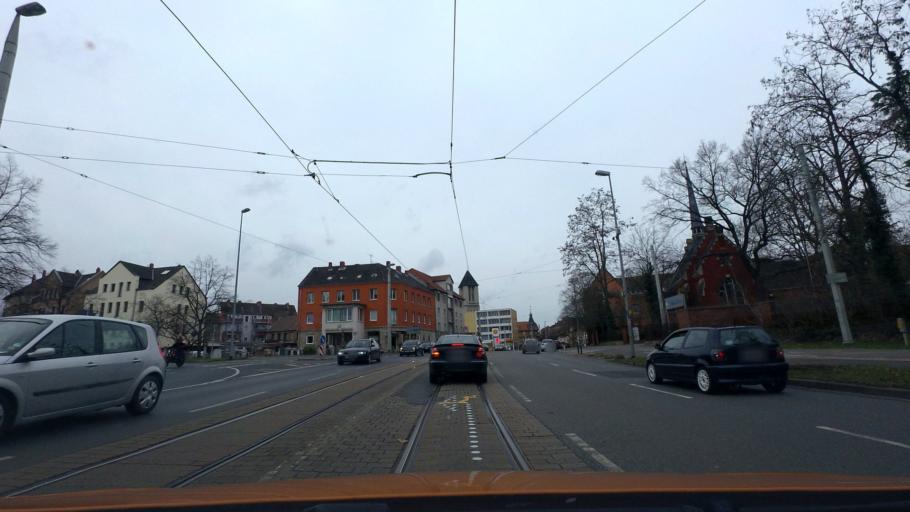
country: DE
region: Lower Saxony
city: Braunschweig
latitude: 52.2574
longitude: 10.5465
